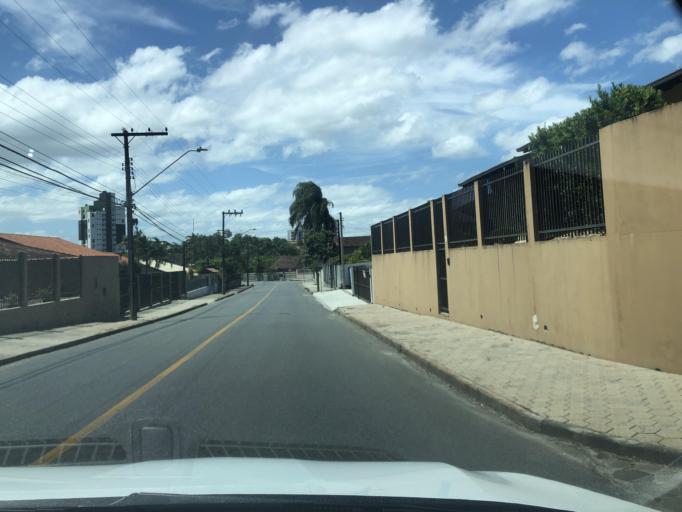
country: BR
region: Santa Catarina
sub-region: Joinville
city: Joinville
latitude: -26.3245
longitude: -48.8523
